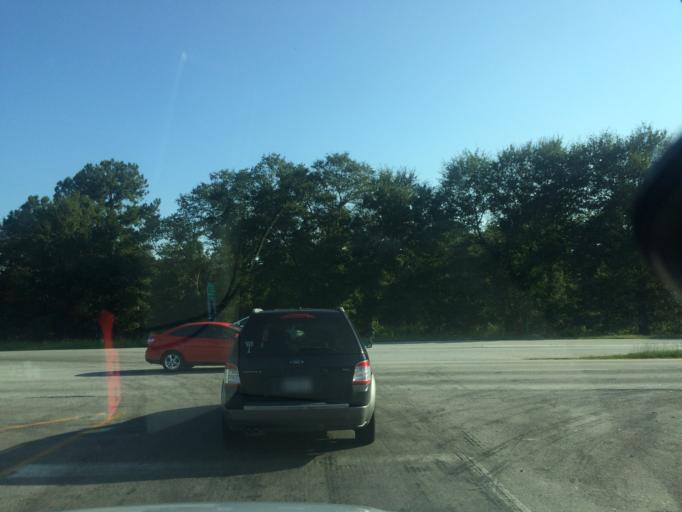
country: US
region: South Carolina
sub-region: Spartanburg County
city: Wellford
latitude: 34.9399
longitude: -82.0765
